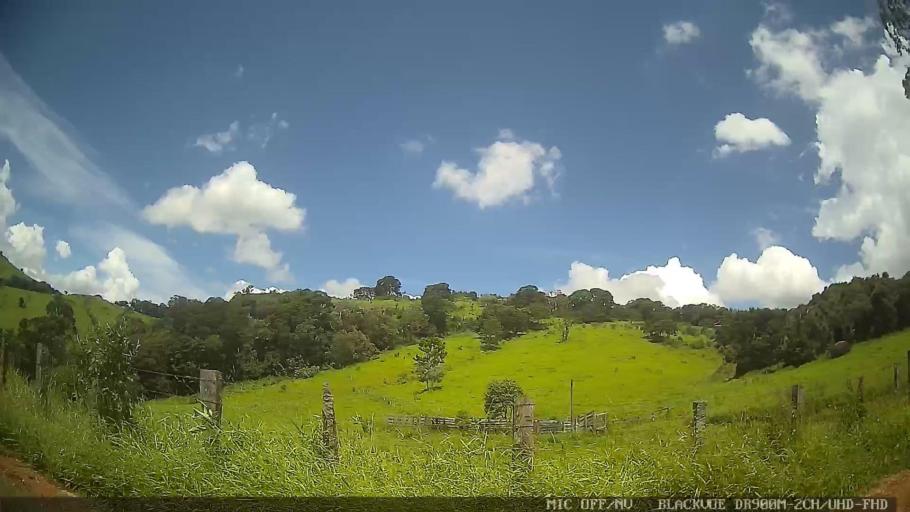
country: BR
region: Minas Gerais
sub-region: Extrema
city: Extrema
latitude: -22.7657
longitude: -46.4369
